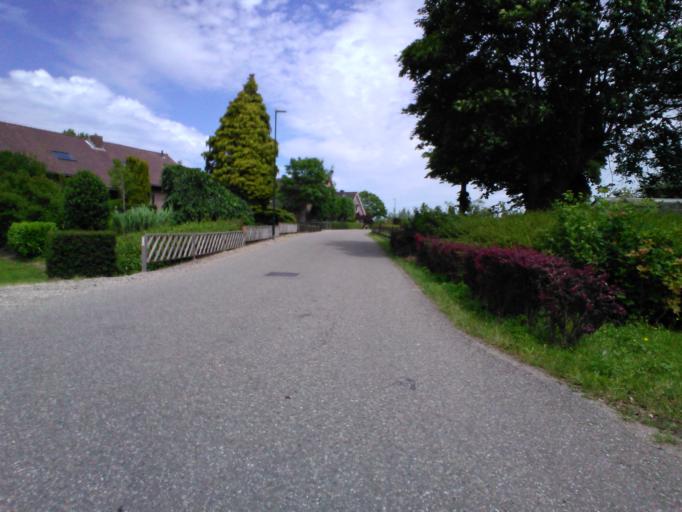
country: NL
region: South Holland
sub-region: Gemeente Giessenlanden
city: Giessenburg
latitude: 51.8467
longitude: 4.8768
